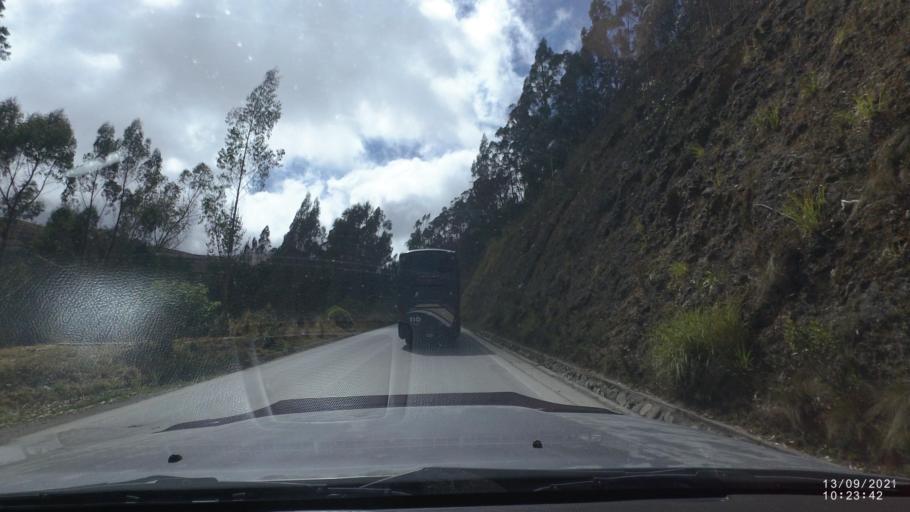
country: BO
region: Cochabamba
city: Colomi
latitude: -17.3178
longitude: -65.8658
